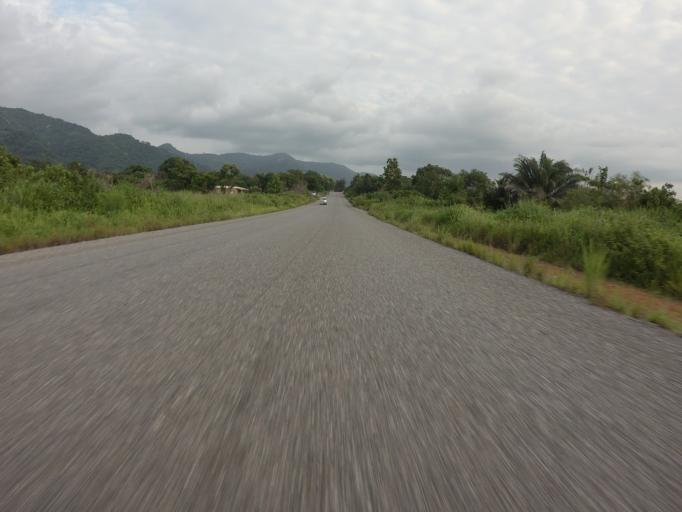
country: GH
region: Volta
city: Kpandu
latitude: 6.8529
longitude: 0.3936
